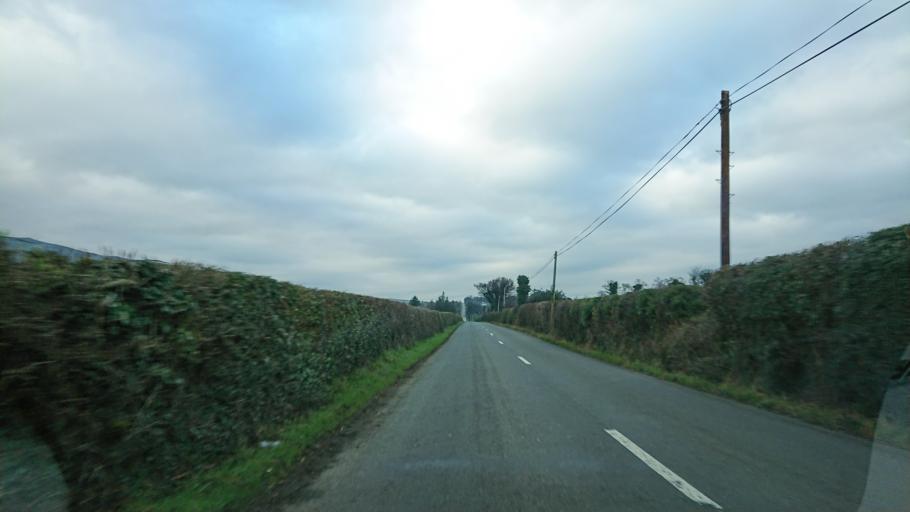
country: IE
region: Munster
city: Carrick-on-Suir
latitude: 52.3170
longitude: -7.5457
